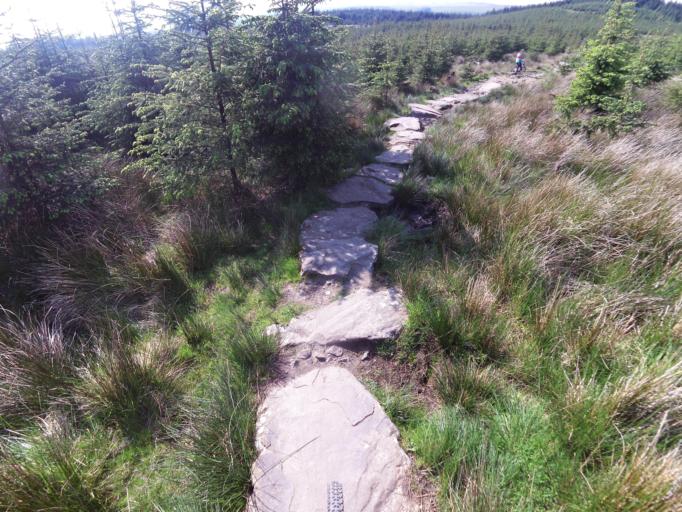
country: GB
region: England
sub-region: North Yorkshire
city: Settle
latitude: 54.0189
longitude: -2.3705
